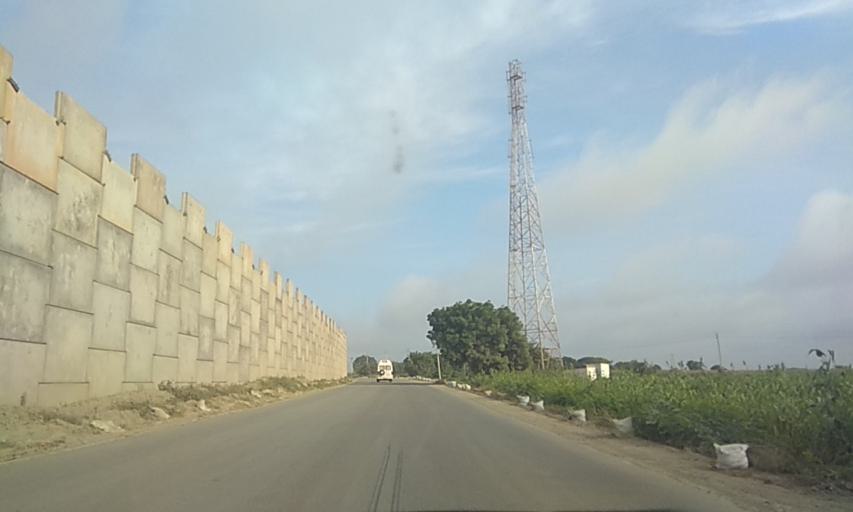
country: IN
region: Karnataka
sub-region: Haveri
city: Haveri
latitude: 14.7587
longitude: 75.4406
